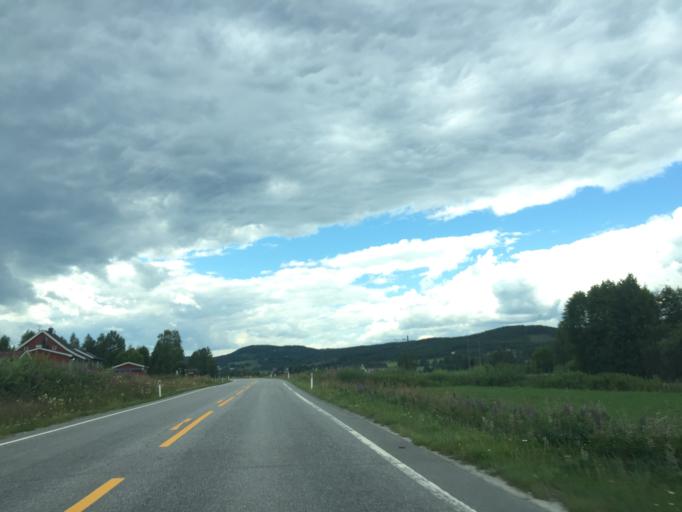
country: NO
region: Hedmark
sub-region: Kongsvinger
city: Kongsvinger
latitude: 60.2002
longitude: 11.9685
